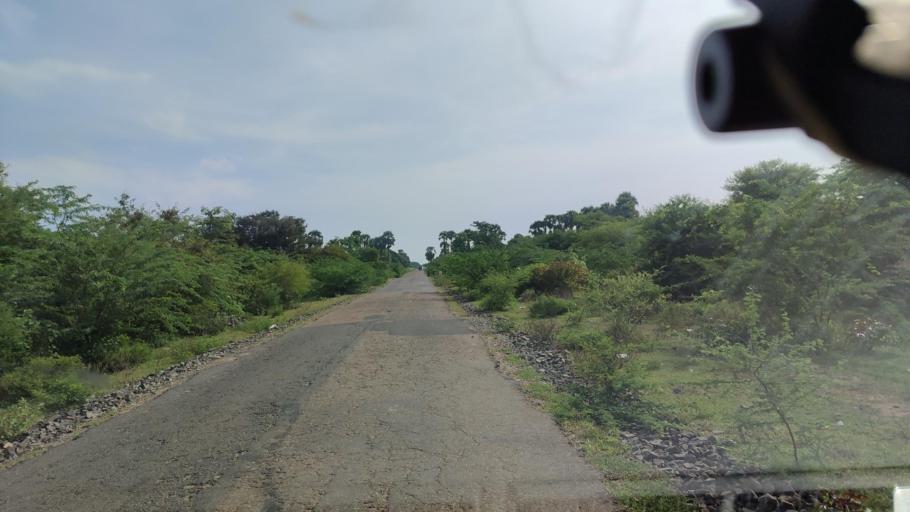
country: MM
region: Mandalay
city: Myingyan
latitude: 21.3385
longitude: 95.2775
